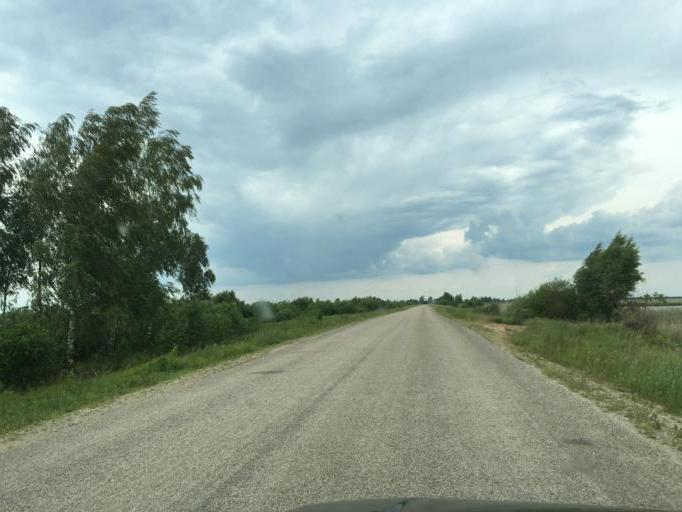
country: LV
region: Vilanu
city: Vilani
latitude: 56.7651
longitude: 26.9694
